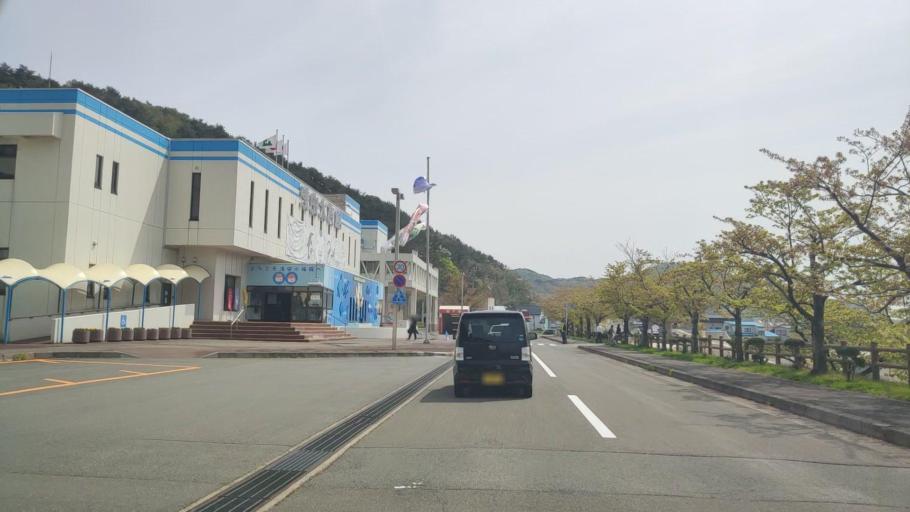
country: JP
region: Aomori
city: Aomori Shi
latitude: 40.8980
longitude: 140.8624
